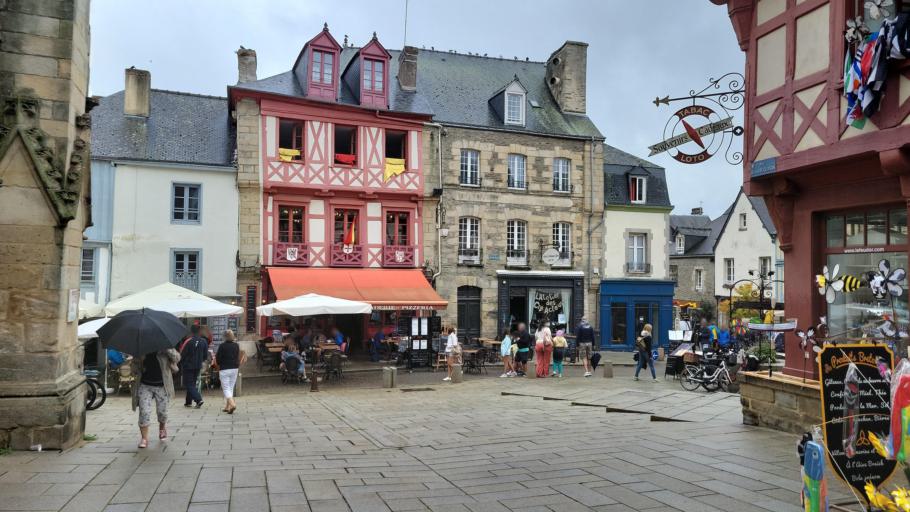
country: FR
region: Brittany
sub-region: Departement du Morbihan
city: Josselin
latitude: 47.9537
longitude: -2.5475
